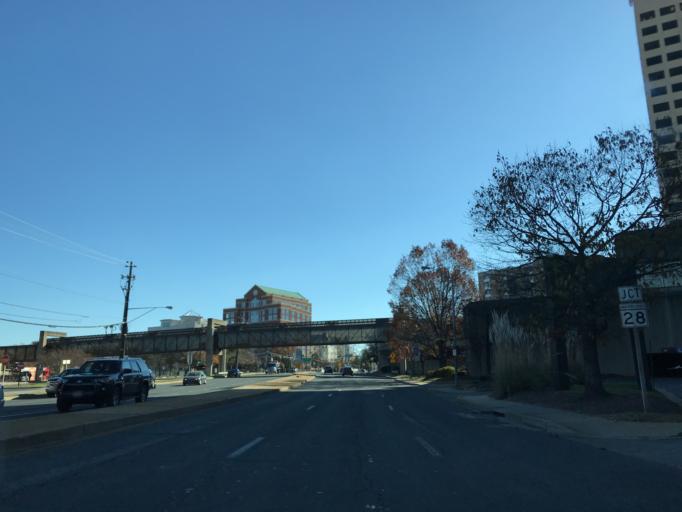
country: US
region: Maryland
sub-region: Montgomery County
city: Rockville
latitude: 39.0850
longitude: -77.1483
